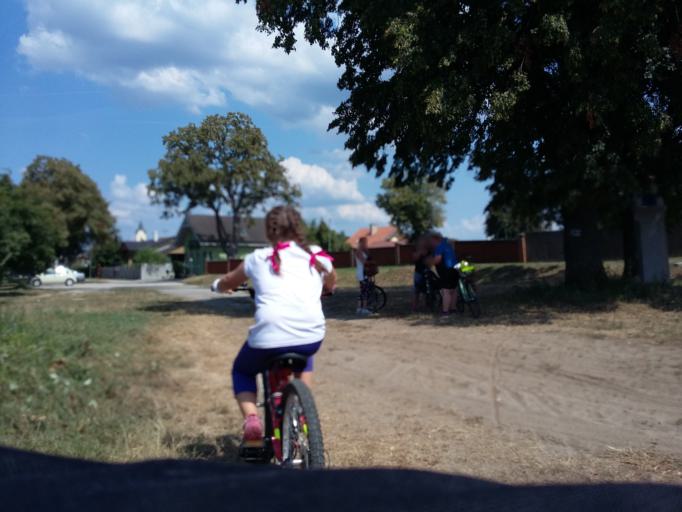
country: SK
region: Bratislavsky
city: Stupava
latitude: 48.3293
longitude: 17.0418
